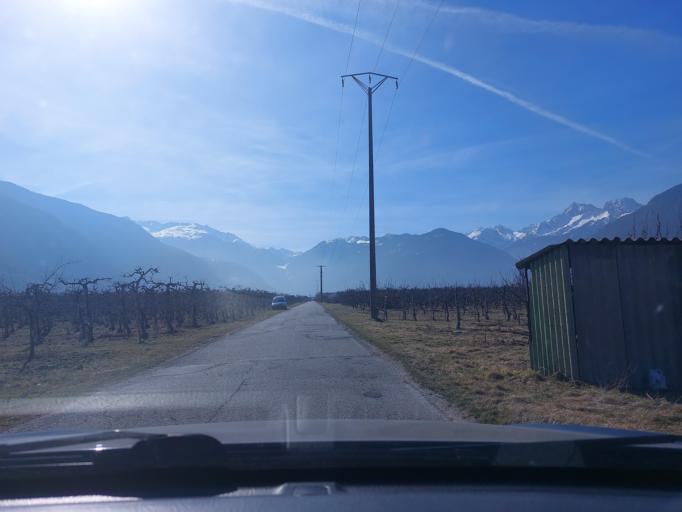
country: CH
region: Valais
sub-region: Martigny District
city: Charrat-les-Chenes
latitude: 46.1338
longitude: 7.1451
